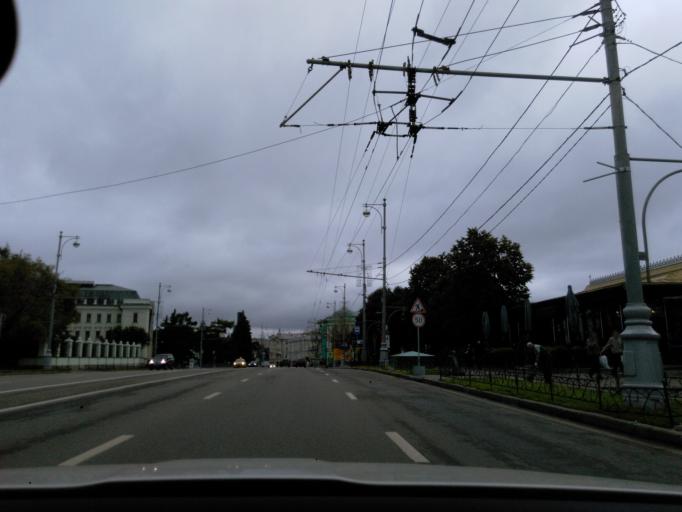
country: RU
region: Moscow
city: Moscow
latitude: 55.7453
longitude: 37.6042
